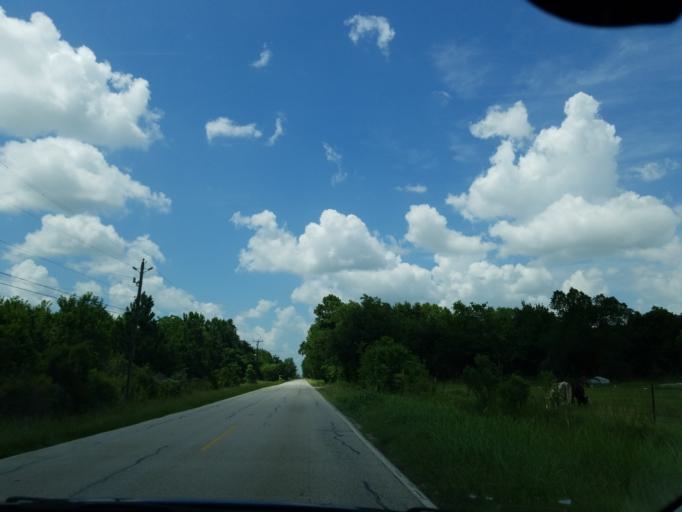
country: US
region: Texas
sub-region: Harris County
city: Katy
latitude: 29.8627
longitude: -95.8071
